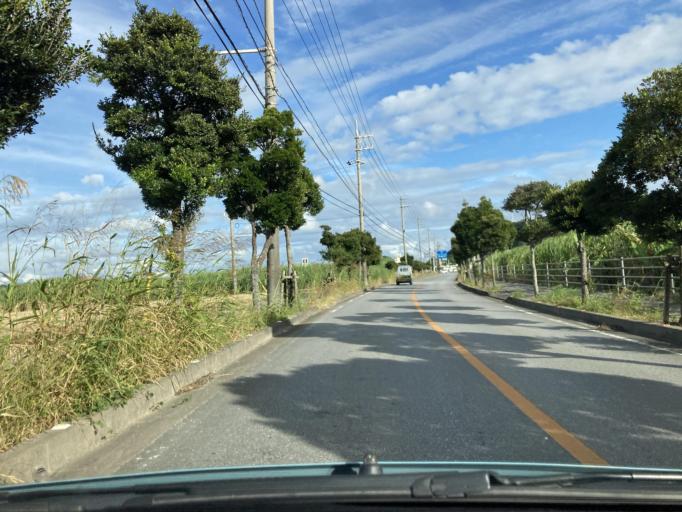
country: JP
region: Okinawa
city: Itoman
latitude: 26.1353
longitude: 127.7073
